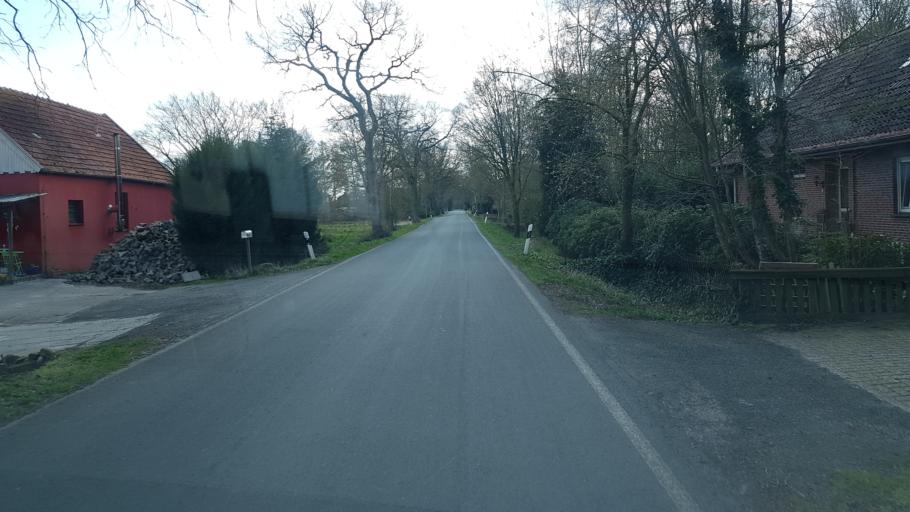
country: DE
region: Lower Saxony
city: Rastede
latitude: 53.3035
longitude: 8.2660
